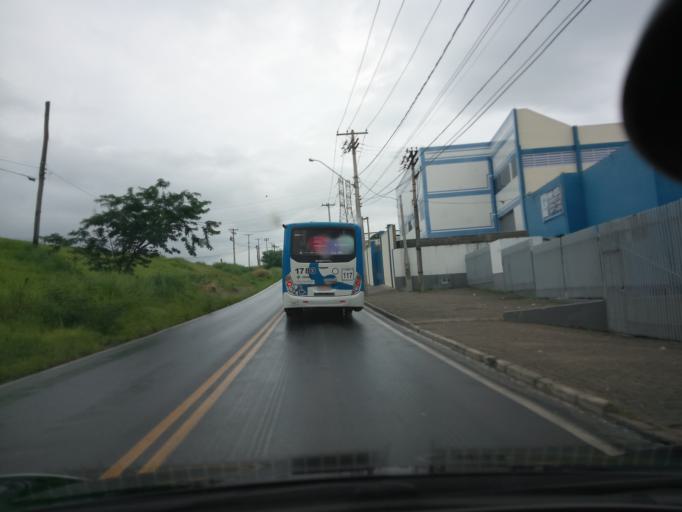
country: BR
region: Sao Paulo
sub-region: Campinas
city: Campinas
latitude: -22.9763
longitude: -47.1038
